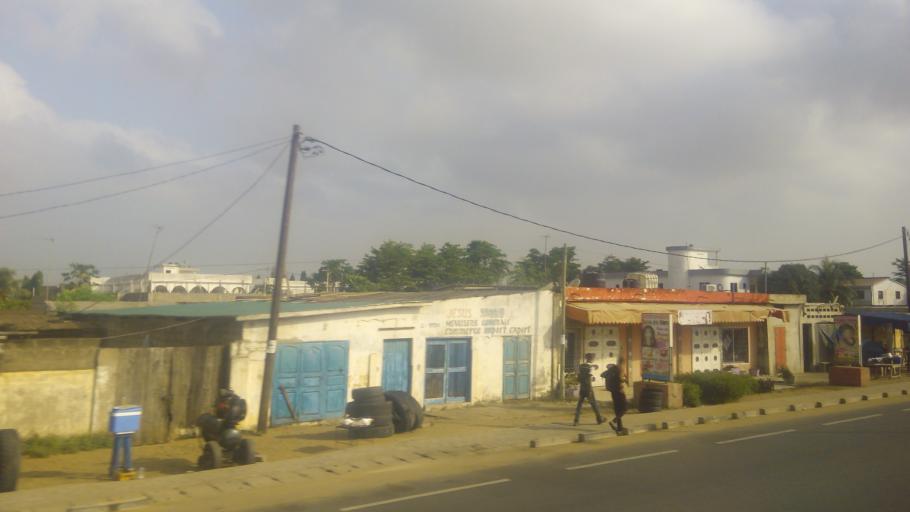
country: TG
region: Maritime
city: Lome
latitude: 6.1674
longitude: 1.3365
